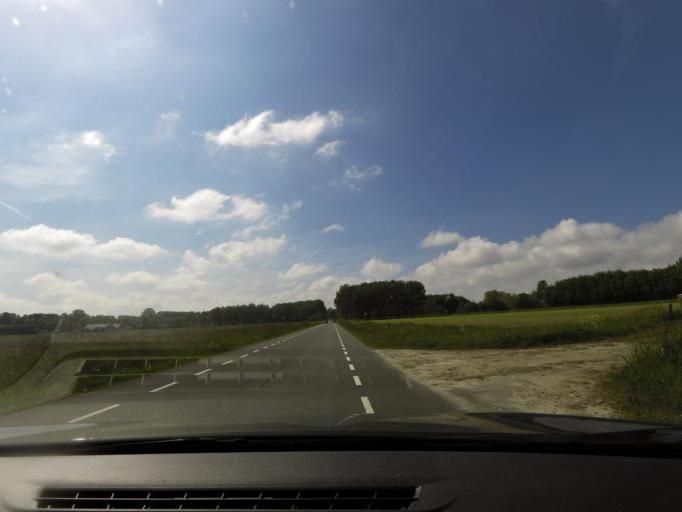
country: NL
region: South Holland
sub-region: Gemeente Hellevoetsluis
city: Nieuw-Helvoet
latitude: 51.8456
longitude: 4.0912
